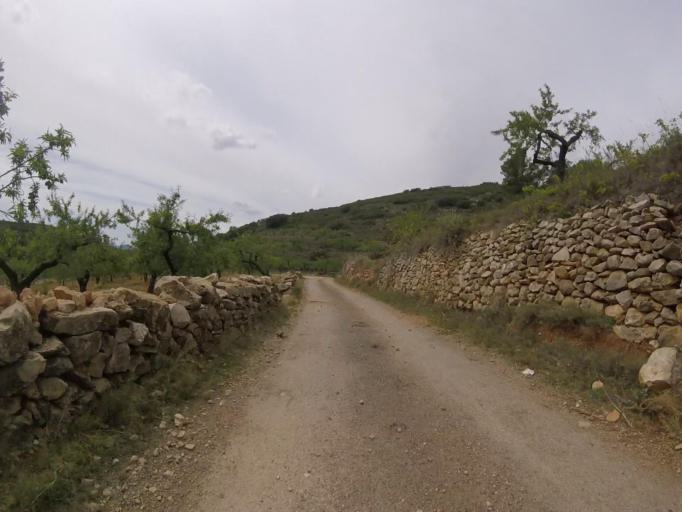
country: ES
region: Valencia
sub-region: Provincia de Castello
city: Sierra-Engarceran
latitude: 40.2553
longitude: -0.0253
